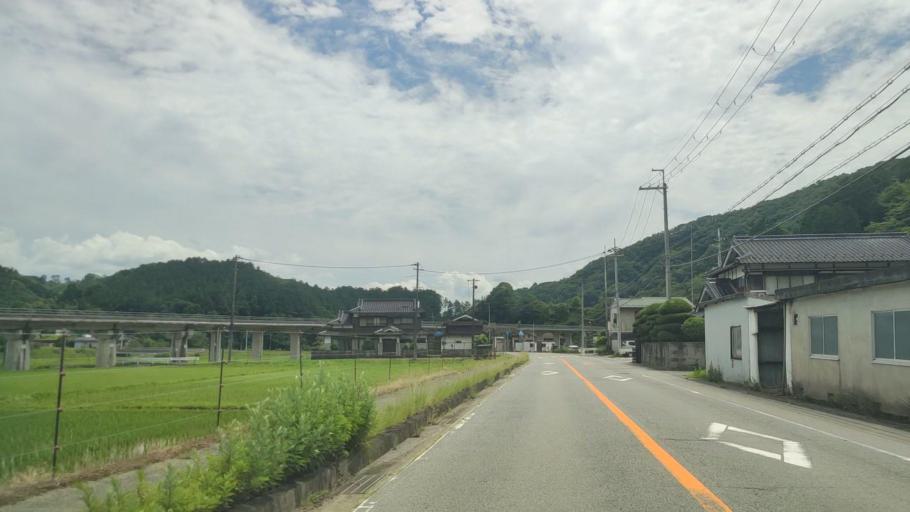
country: JP
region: Hyogo
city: Yamazakicho-nakabirose
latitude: 35.0366
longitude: 134.3676
